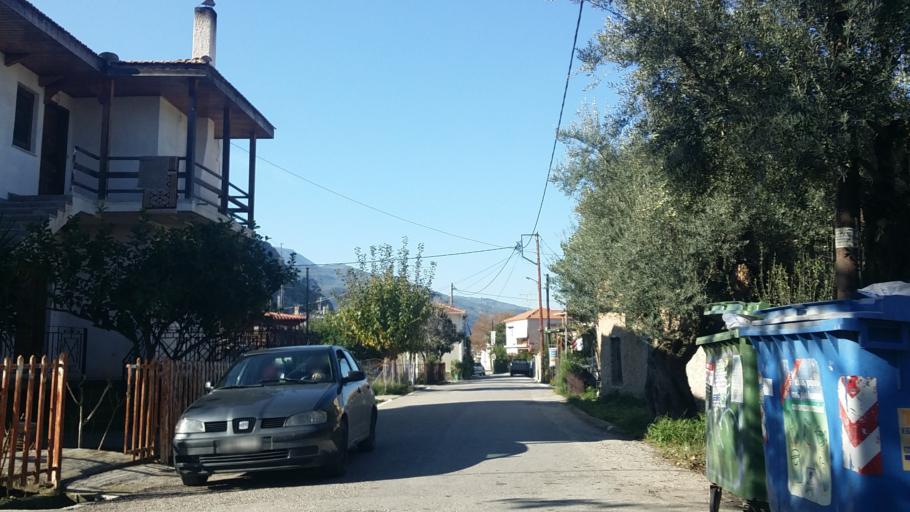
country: GR
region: West Greece
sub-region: Nomos Achaias
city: Temeni
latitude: 38.1873
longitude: 22.1849
